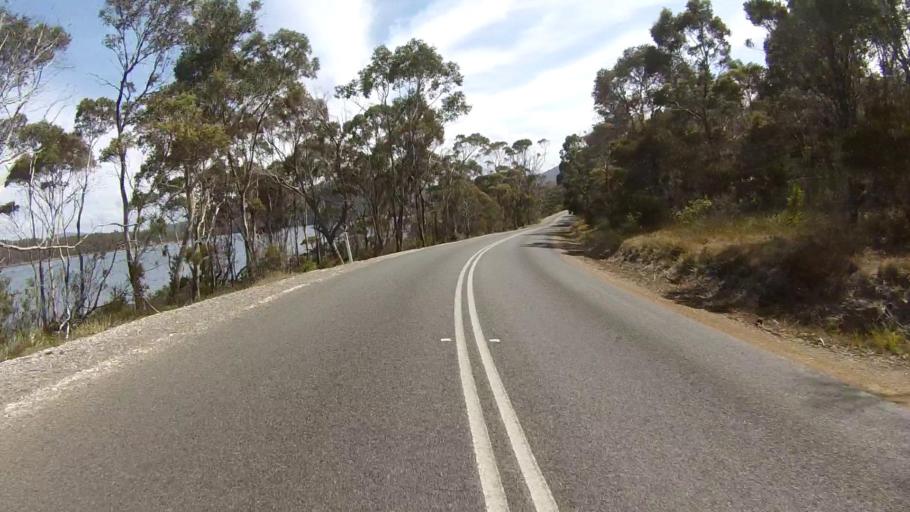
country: AU
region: Tasmania
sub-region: Huon Valley
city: Cygnet
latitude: -43.2655
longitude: 147.1427
